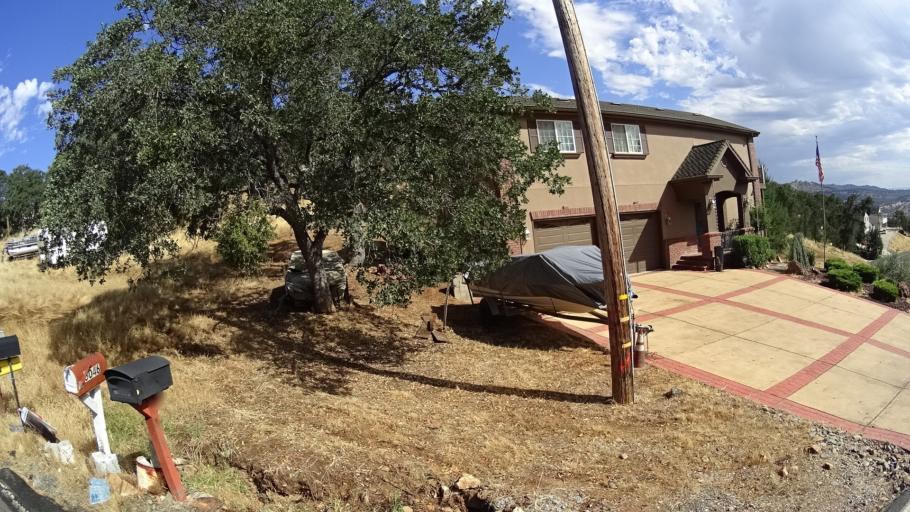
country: US
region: California
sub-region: Calaveras County
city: Copperopolis
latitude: 37.9083
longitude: -120.6100
